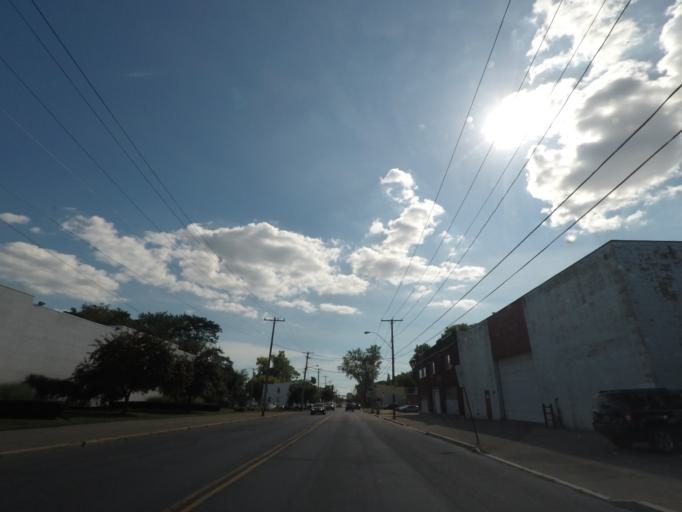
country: US
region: New York
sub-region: Albany County
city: Menands
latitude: 42.6742
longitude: -73.7369
